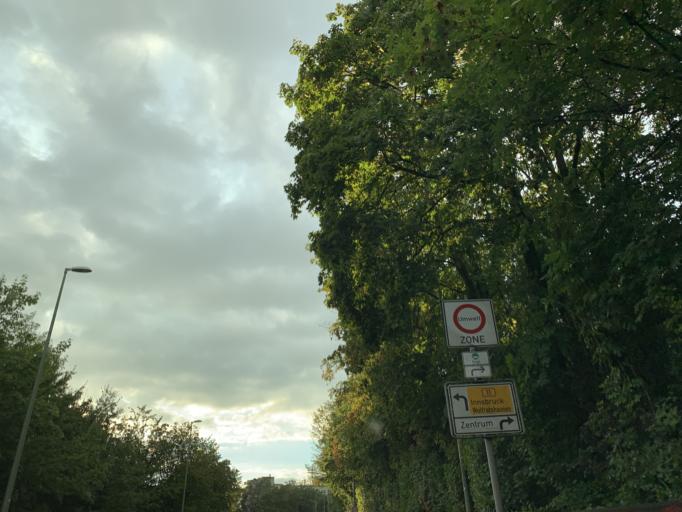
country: DE
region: Bavaria
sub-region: Upper Bavaria
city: Munich
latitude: 48.1123
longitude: 11.5413
